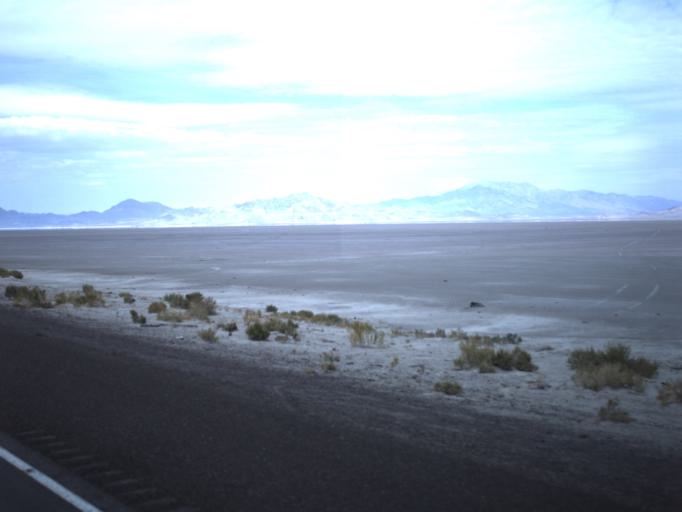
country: US
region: Utah
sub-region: Tooele County
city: Wendover
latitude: 40.7370
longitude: -113.7367
